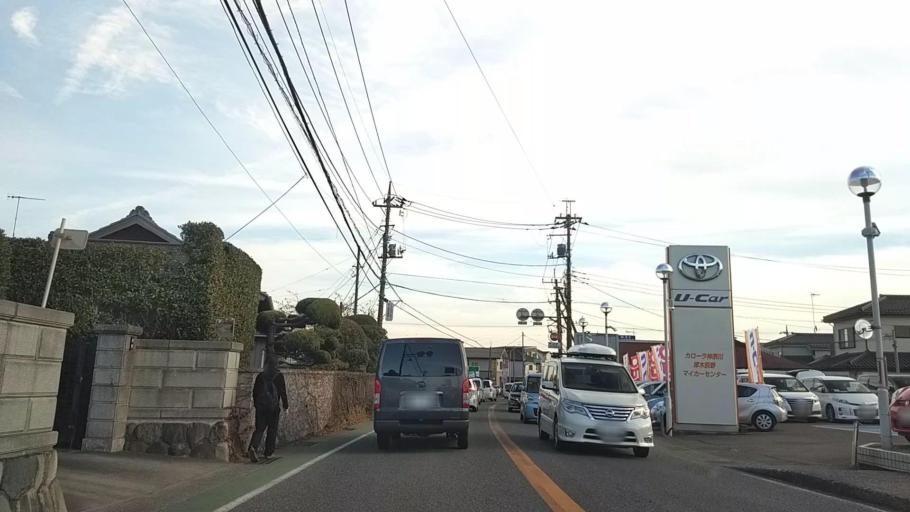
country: JP
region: Kanagawa
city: Atsugi
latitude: 35.4781
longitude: 139.3420
